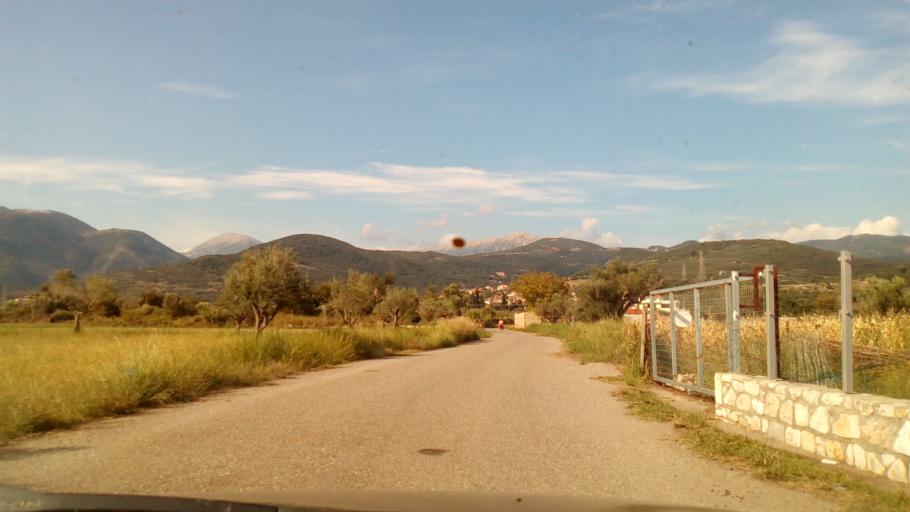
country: GR
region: West Greece
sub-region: Nomos Aitolias kai Akarnanias
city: Nafpaktos
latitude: 38.4055
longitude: 21.8962
